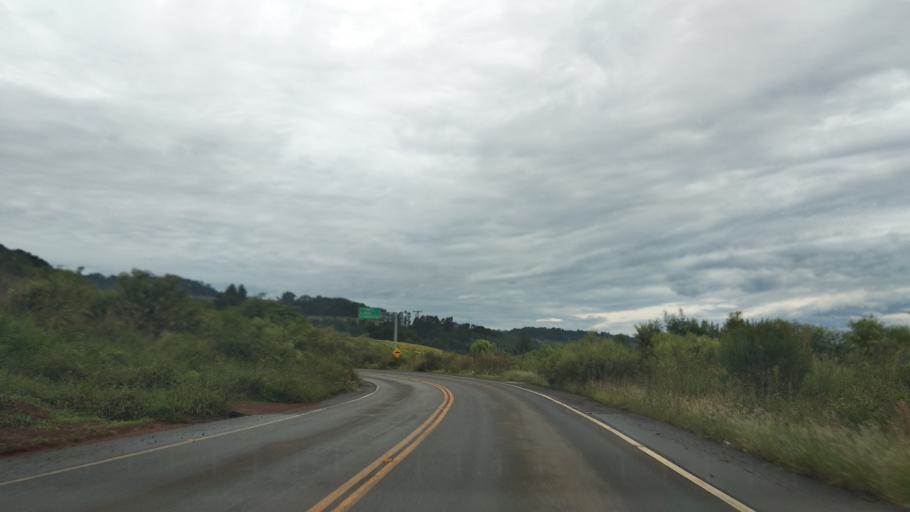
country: BR
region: Santa Catarina
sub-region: Videira
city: Videira
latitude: -27.0140
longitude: -51.1683
